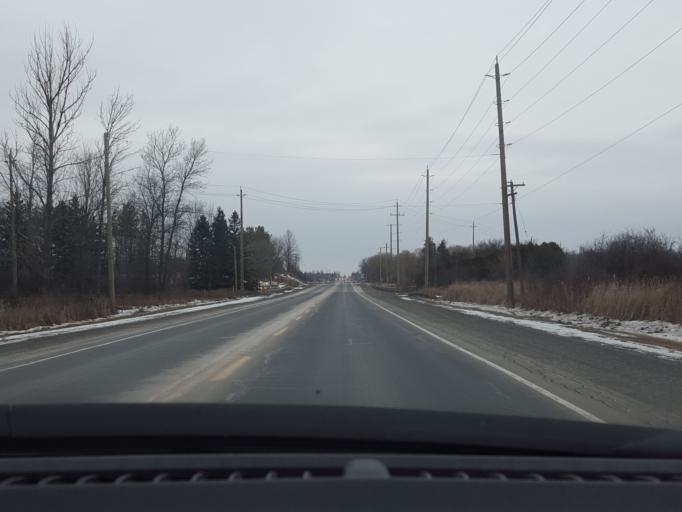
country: CA
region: Ontario
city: Keswick
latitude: 44.1856
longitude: -79.4364
